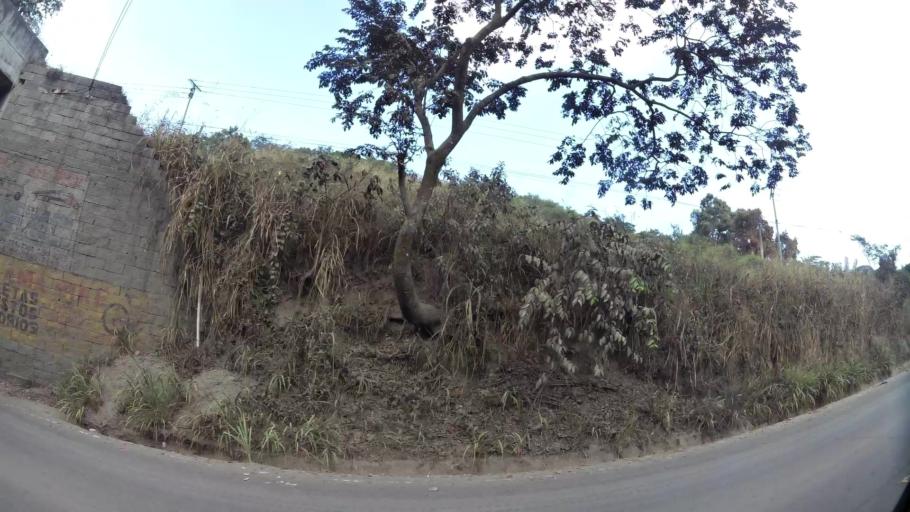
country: SV
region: San Salvador
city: Delgado
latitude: 13.7213
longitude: -89.1582
